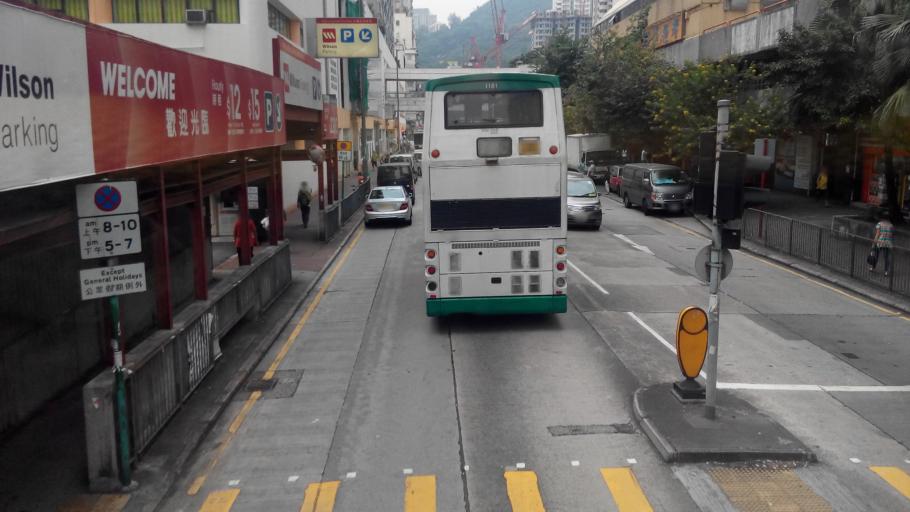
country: HK
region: Sham Shui Po
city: Sham Shui Po
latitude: 22.3380
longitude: 114.1587
